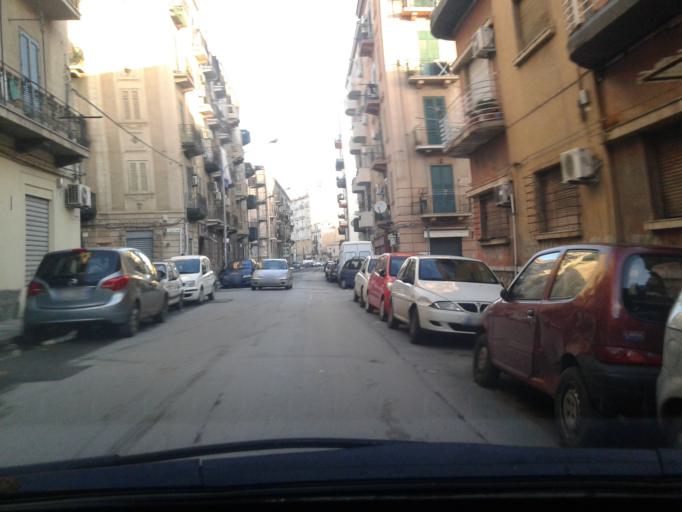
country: IT
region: Sicily
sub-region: Palermo
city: Palermo
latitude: 38.1148
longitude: 13.3456
